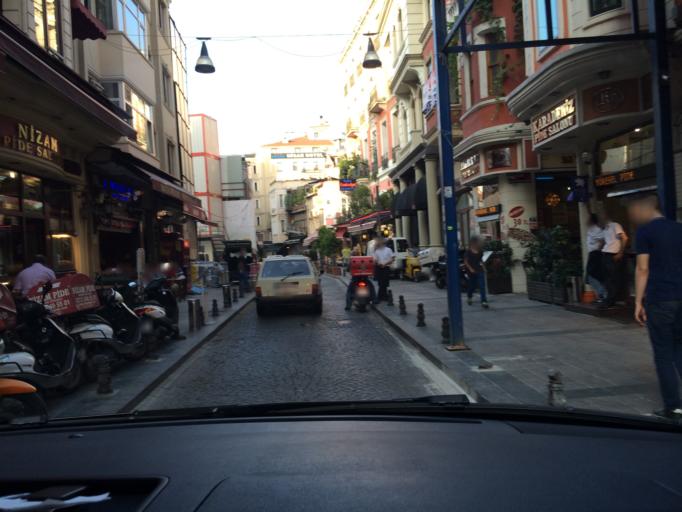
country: TR
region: Istanbul
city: Eminoenue
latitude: 41.0345
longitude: 28.9765
